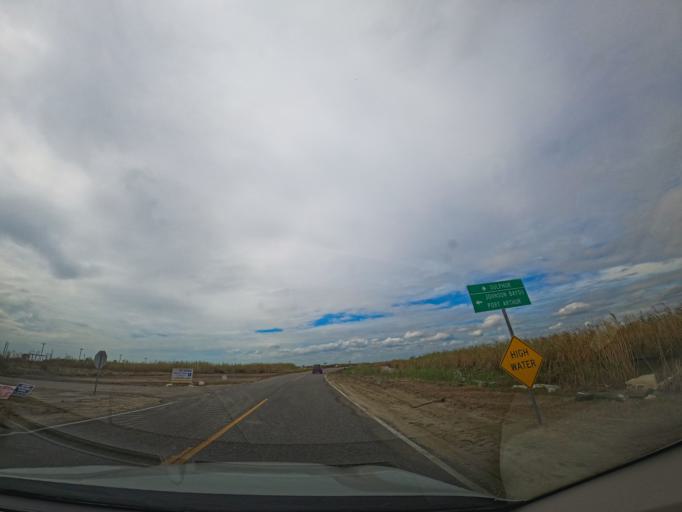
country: US
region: Louisiana
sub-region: Cameron Parish
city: Cameron
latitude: 29.7722
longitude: -93.4595
